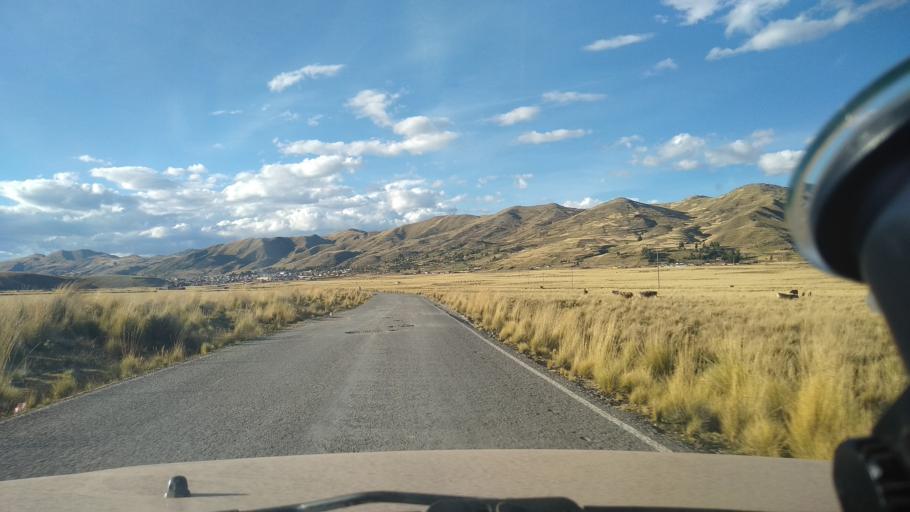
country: PE
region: Cusco
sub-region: Provincia de Canas
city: Chignayhua
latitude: -14.2431
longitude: -71.4334
